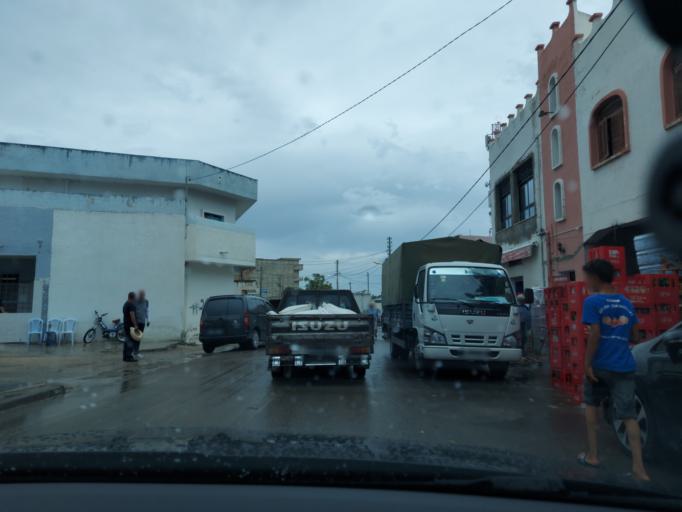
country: TN
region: Silyanah
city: Maktar
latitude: 35.8568
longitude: 9.2034
